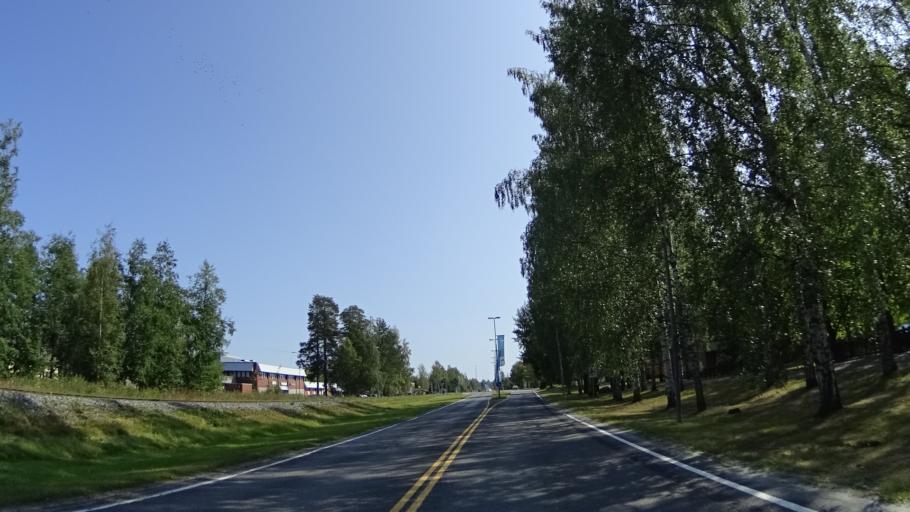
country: FI
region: Pirkanmaa
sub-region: Ylae-Pirkanmaa
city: Maenttae
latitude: 62.0300
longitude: 24.6190
